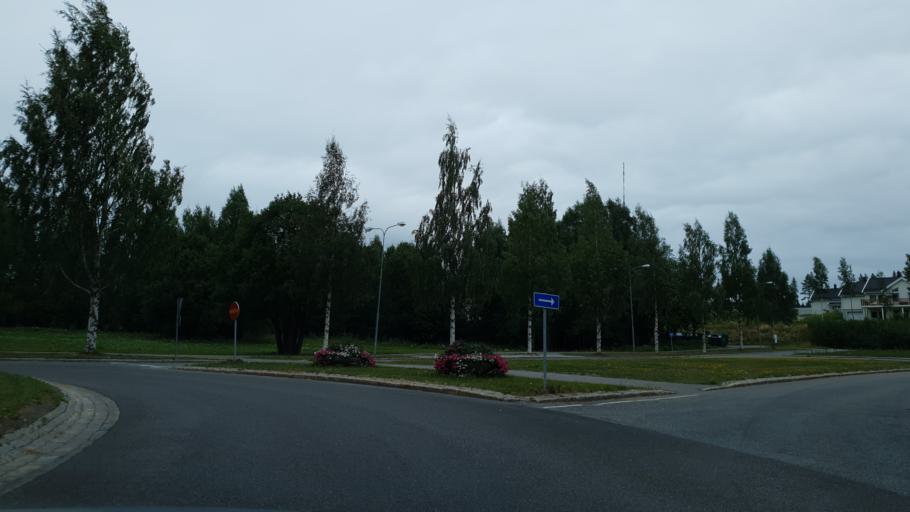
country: SE
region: Vaesterbotten
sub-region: Skelleftea Kommun
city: Skelleftea
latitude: 64.7612
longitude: 20.9521
